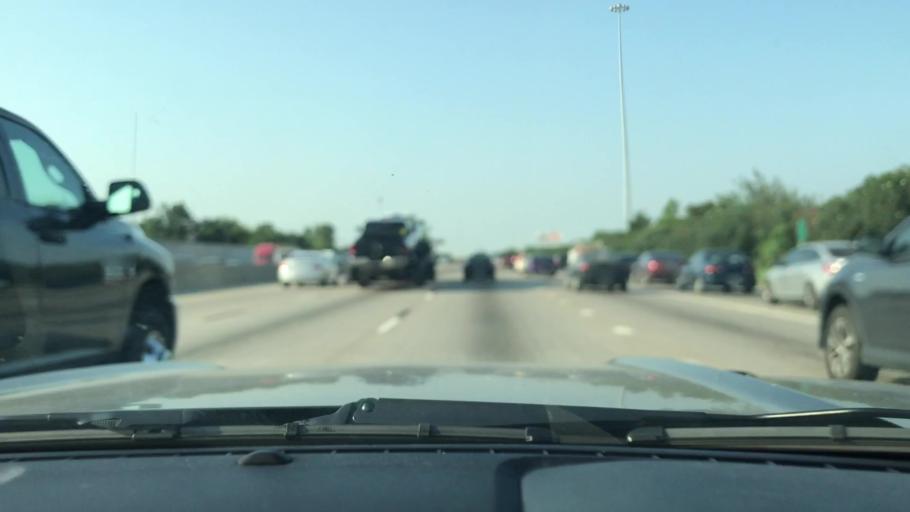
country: US
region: Texas
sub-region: Harris County
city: Jacinto City
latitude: 29.7622
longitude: -95.2652
